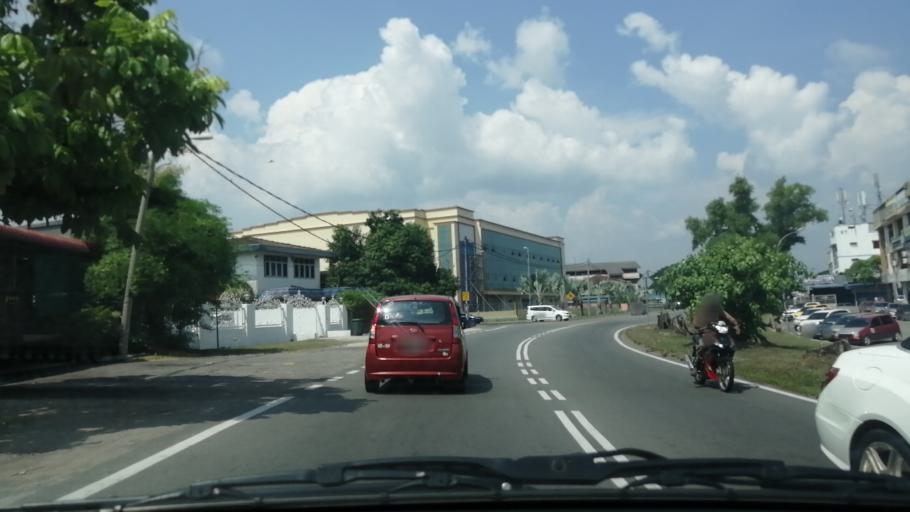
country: MY
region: Kedah
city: Sungai Petani
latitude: 5.6453
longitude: 100.4965
